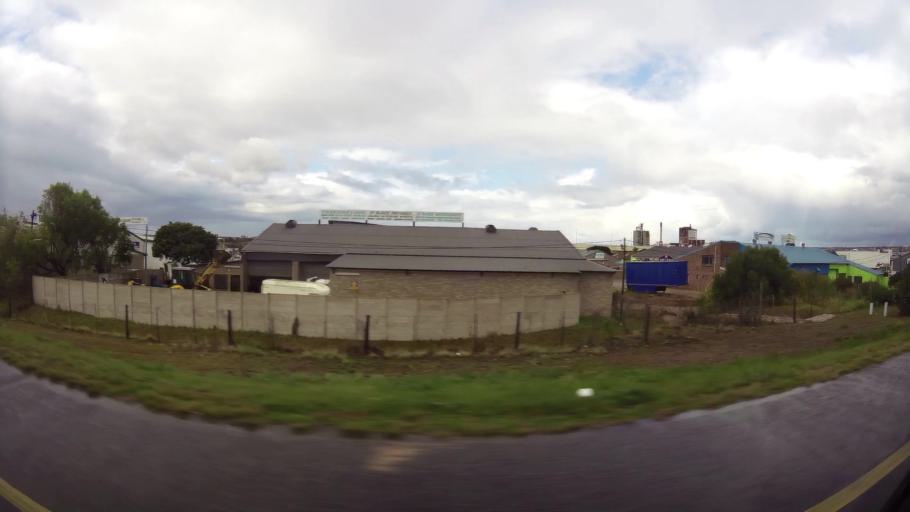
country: ZA
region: Western Cape
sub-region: Eden District Municipality
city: Mossel Bay
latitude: -34.1429
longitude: 22.1002
